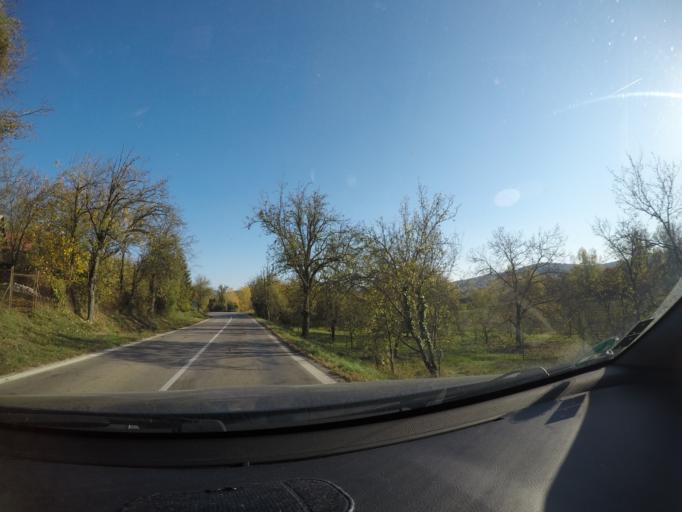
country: SK
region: Trenciansky
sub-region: Okres Trencin
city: Trencin
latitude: 48.9060
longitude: 18.0618
